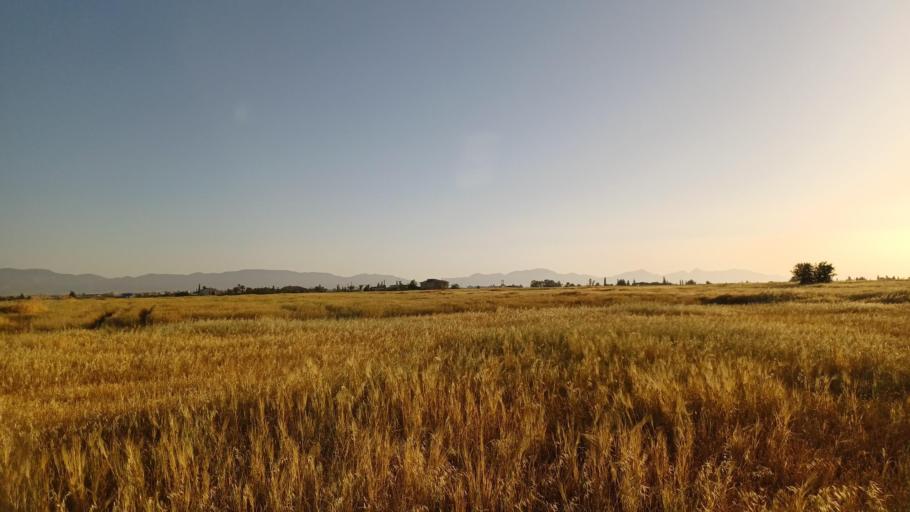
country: CY
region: Lefkosia
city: Kokkinotrimithia
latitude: 35.1420
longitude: 33.1870
